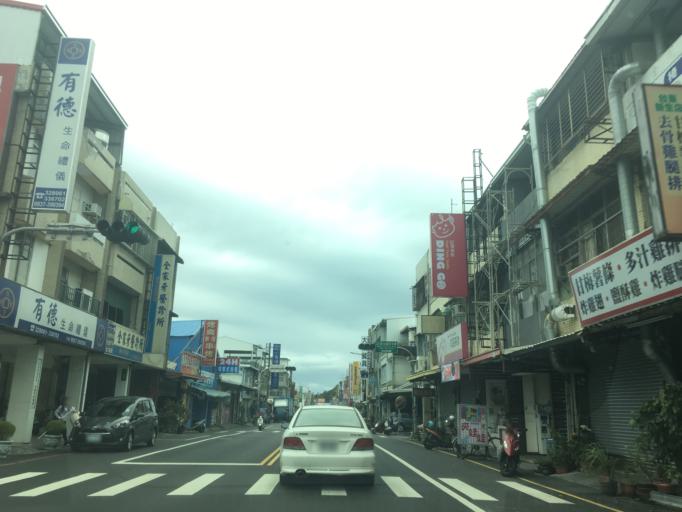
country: TW
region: Taiwan
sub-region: Taitung
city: Taitung
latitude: 22.7632
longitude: 121.1363
